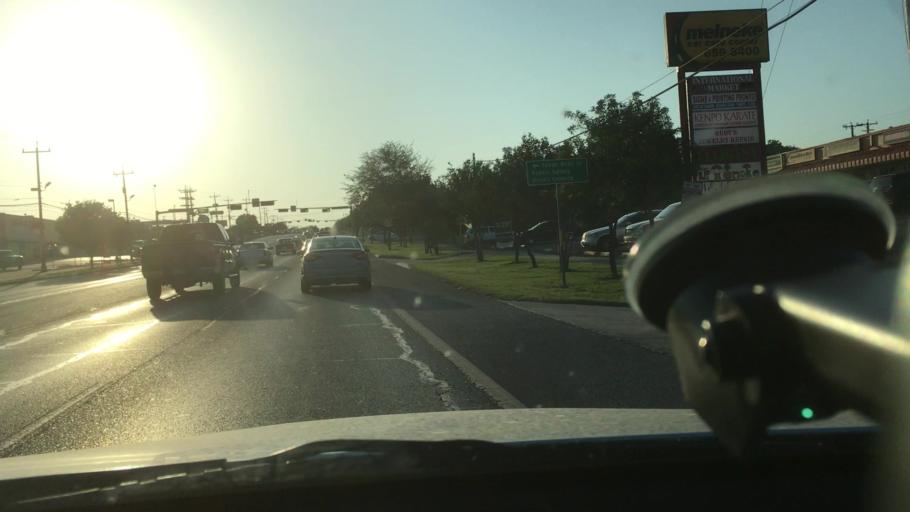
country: US
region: Texas
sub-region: Bexar County
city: Universal City
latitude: 29.5523
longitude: -98.3053
